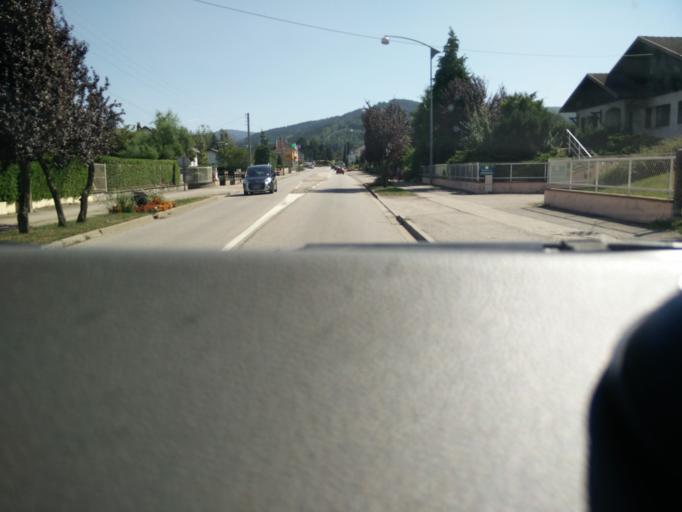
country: FR
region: Lorraine
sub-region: Departement des Vosges
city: Anould
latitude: 48.1913
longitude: 6.9513
